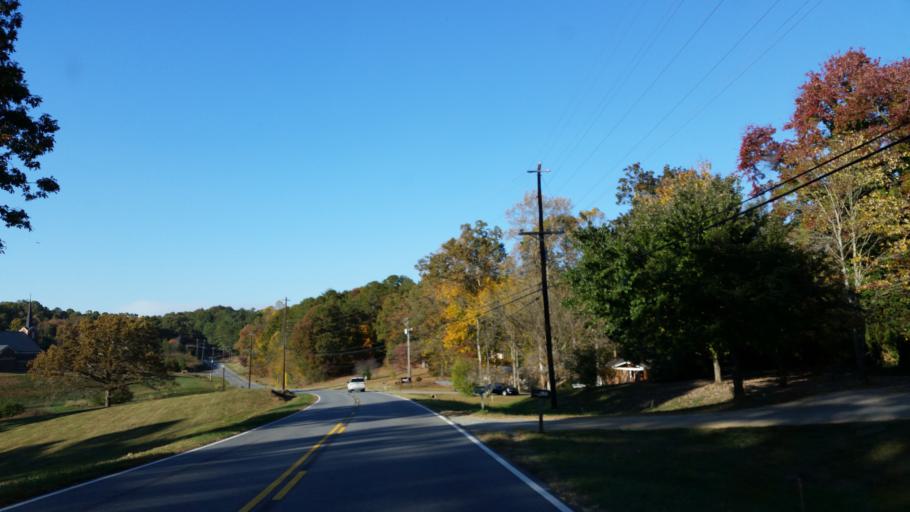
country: US
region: Georgia
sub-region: Gilmer County
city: Ellijay
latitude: 34.6652
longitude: -84.4731
